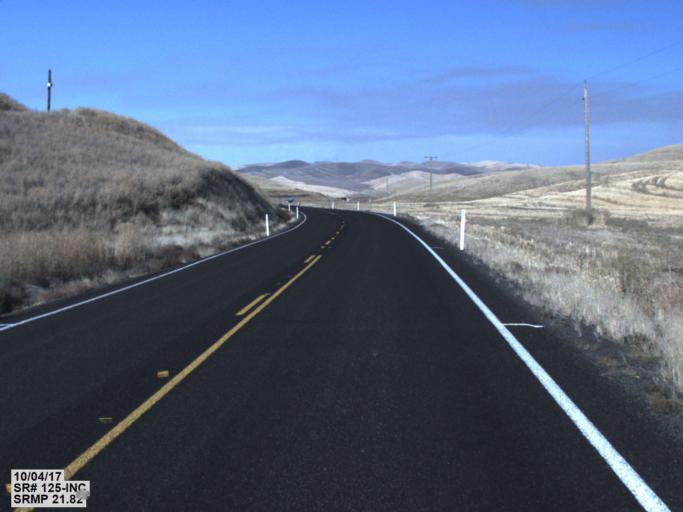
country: US
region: Washington
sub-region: Walla Walla County
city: Waitsburg
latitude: 46.2732
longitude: -118.3481
